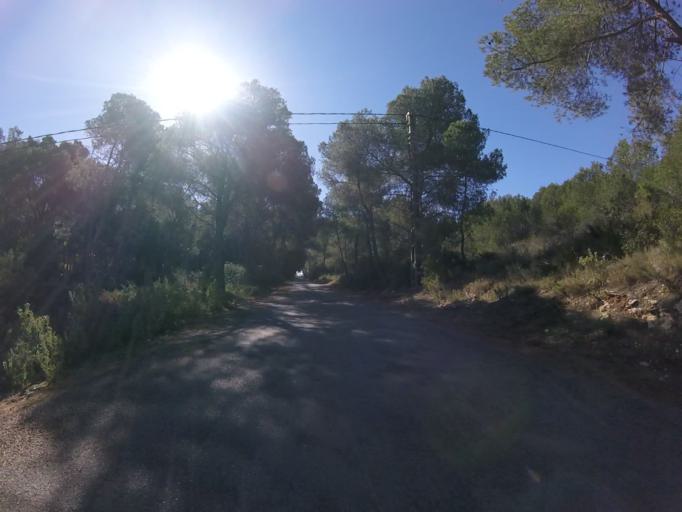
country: ES
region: Valencia
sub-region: Provincia de Castello
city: Orpesa/Oropesa del Mar
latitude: 40.0760
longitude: 0.1173
